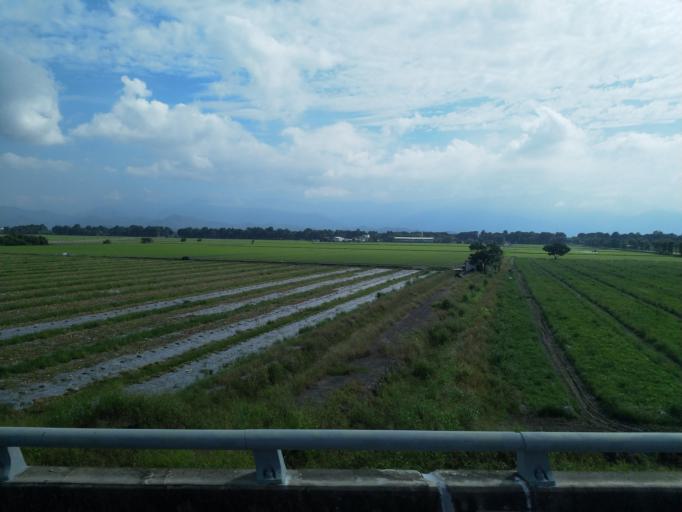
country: TW
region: Taiwan
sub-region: Pingtung
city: Pingtung
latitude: 22.8466
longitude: 120.4956
